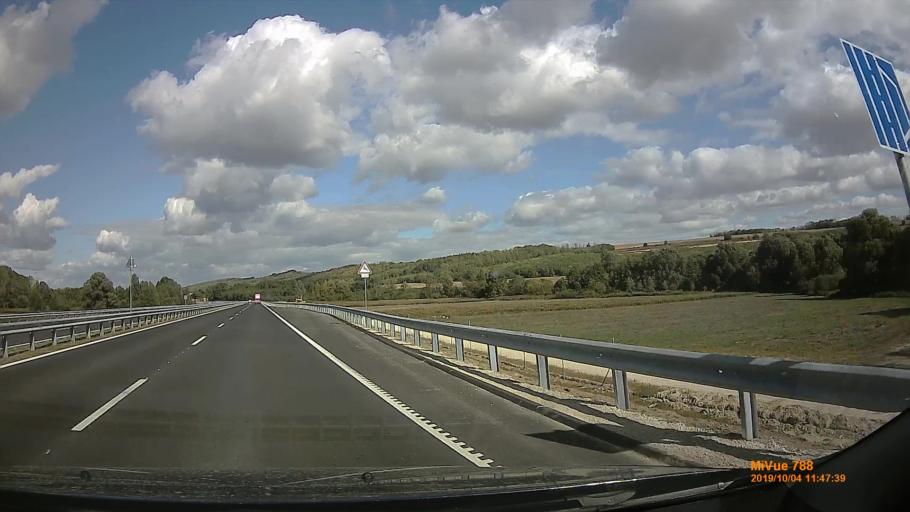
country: HU
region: Somogy
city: Karad
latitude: 46.6517
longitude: 17.7863
